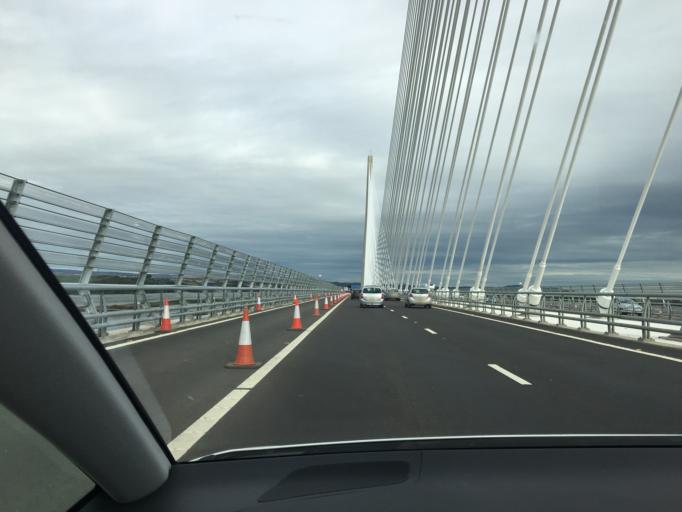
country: GB
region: Scotland
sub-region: Edinburgh
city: Queensferry
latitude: 56.0053
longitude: -3.4131
